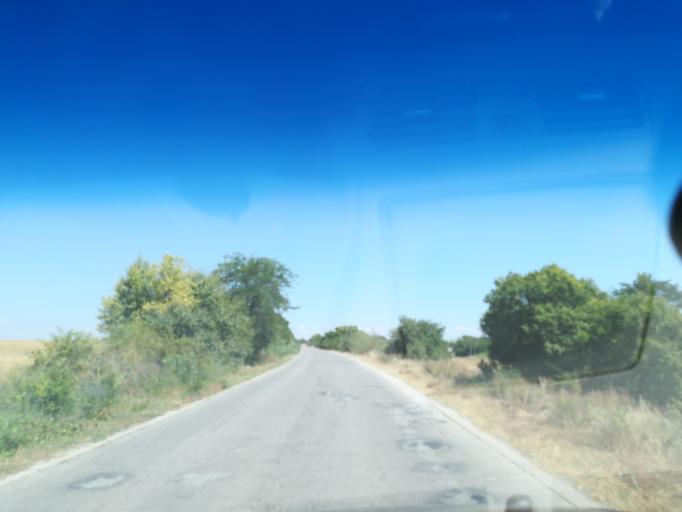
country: BG
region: Plovdiv
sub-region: Obshtina Sadovo
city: Sadovo
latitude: 42.0243
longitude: 24.9954
